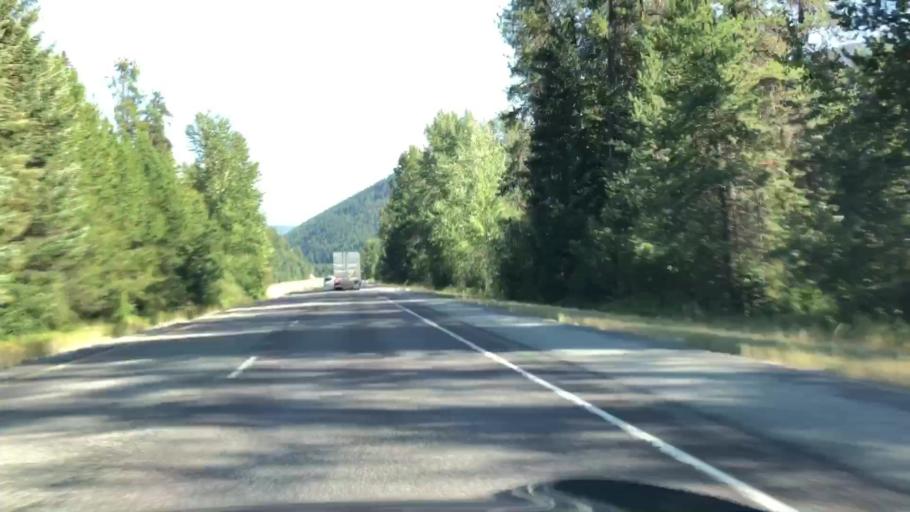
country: US
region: Montana
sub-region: Sanders County
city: Thompson Falls
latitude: 47.3663
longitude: -115.3307
